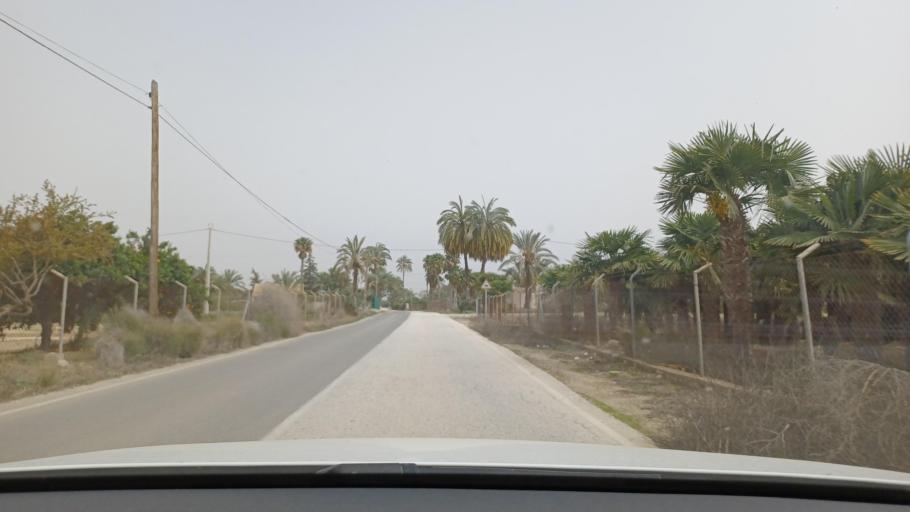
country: ES
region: Valencia
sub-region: Provincia de Alicante
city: Elche
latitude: 38.2350
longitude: -0.6931
